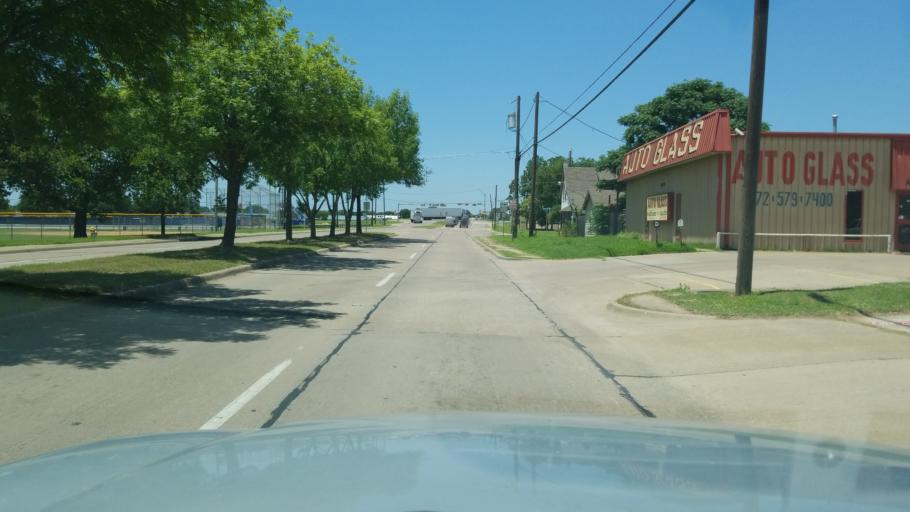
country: US
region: Texas
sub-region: Dallas County
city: Irving
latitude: 32.8013
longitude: -96.9184
